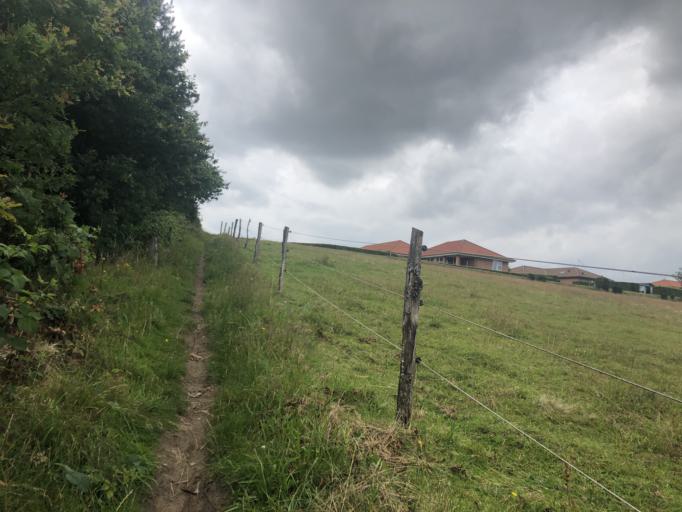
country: DK
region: South Denmark
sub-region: Kolding Kommune
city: Kolding
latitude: 55.5600
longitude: 9.4184
